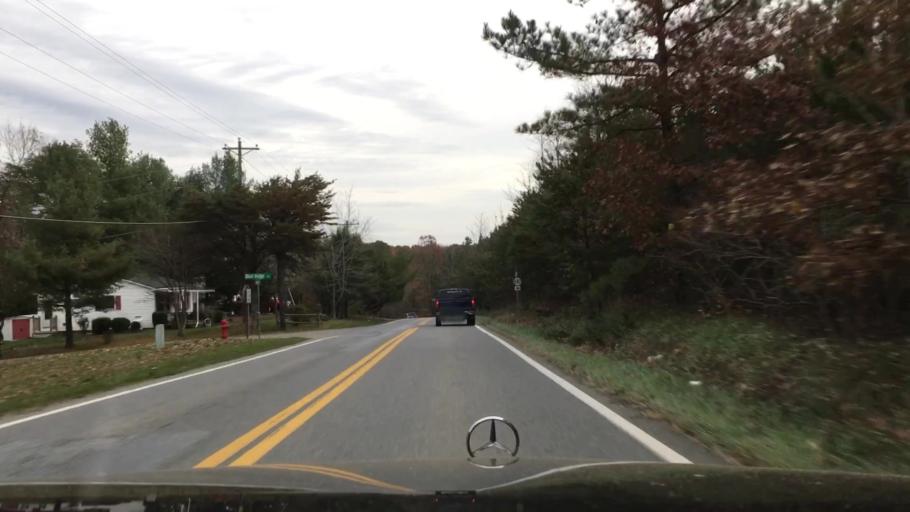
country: US
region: Virginia
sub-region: Campbell County
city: Timberlake
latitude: 37.2640
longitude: -79.2666
